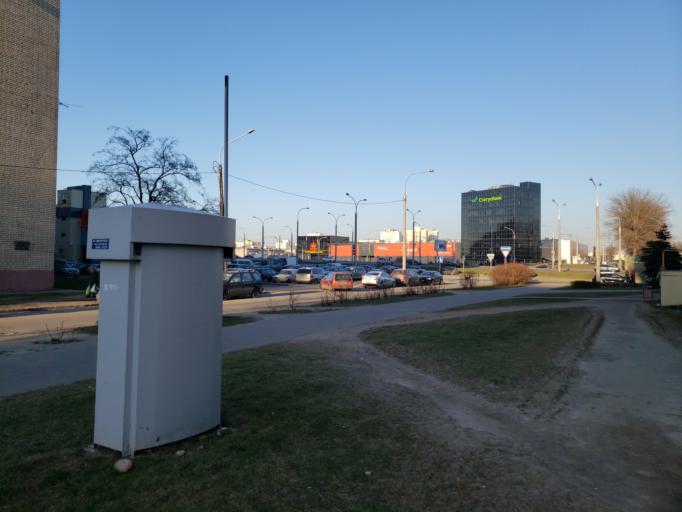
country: BY
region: Minsk
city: Minsk
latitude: 53.8703
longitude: 27.5684
